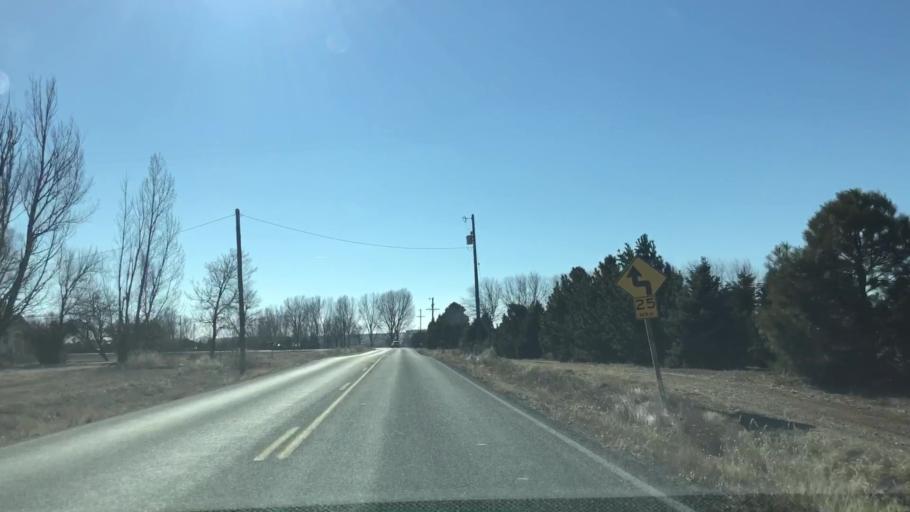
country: US
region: Colorado
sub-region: Weld County
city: Windsor
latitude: 40.4922
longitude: -104.9441
